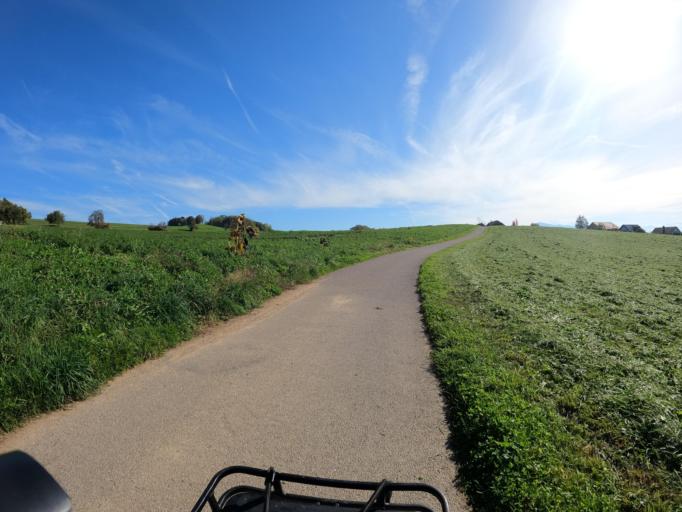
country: CH
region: Zurich
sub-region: Bezirk Affoltern
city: Mettmenstetten
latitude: 47.2443
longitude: 8.4700
